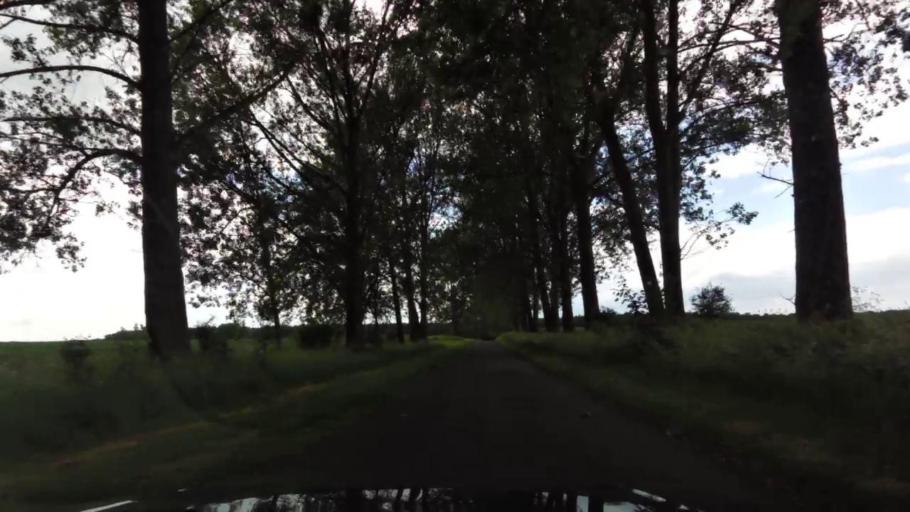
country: PL
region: West Pomeranian Voivodeship
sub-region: Powiat mysliborski
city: Mysliborz
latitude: 52.9897
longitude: 14.7613
